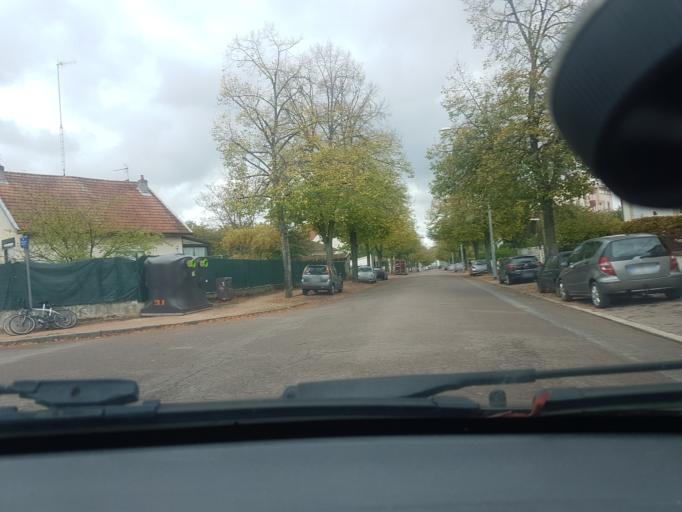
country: FR
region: Bourgogne
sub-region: Departement de la Cote-d'Or
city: Longvic
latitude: 47.3110
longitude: 5.0583
